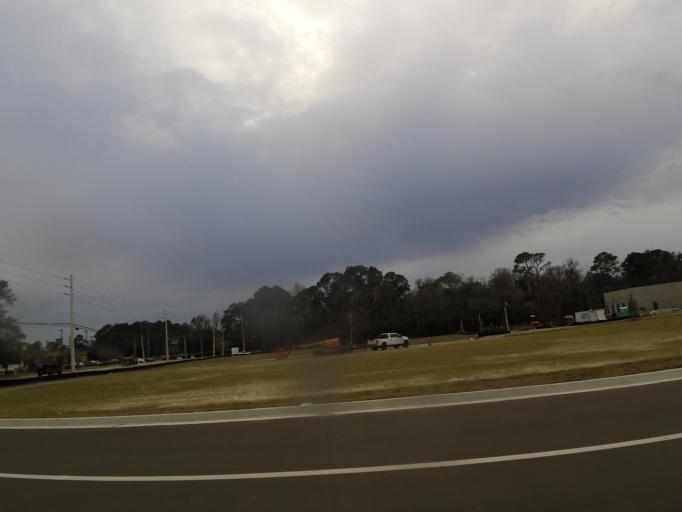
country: US
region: Florida
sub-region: Duval County
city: Jacksonville
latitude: 30.4616
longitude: -81.5773
